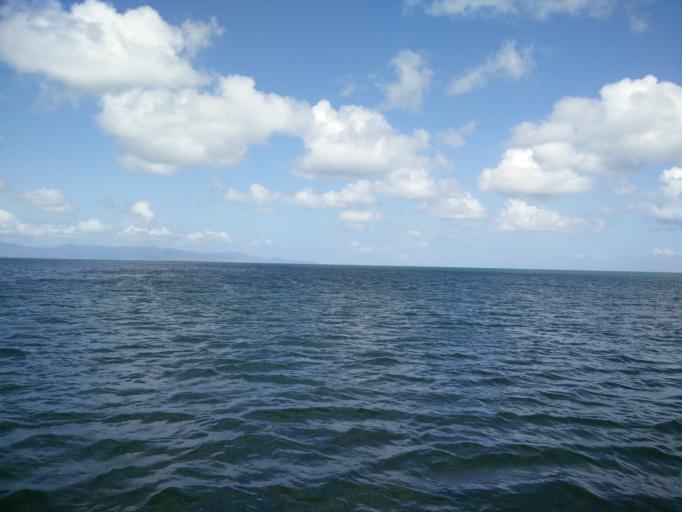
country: GP
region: Guadeloupe
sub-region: Guadeloupe
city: Petit-Canal
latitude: 16.3764
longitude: -61.4989
